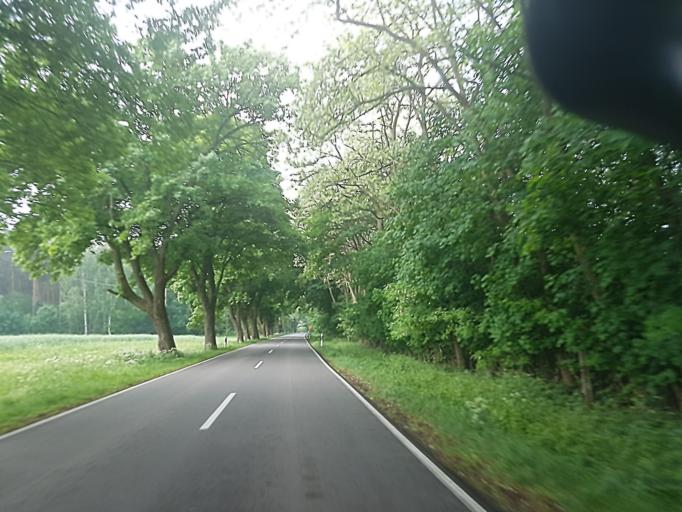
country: DE
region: Saxony-Anhalt
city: Klieken
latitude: 51.9916
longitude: 12.3601
